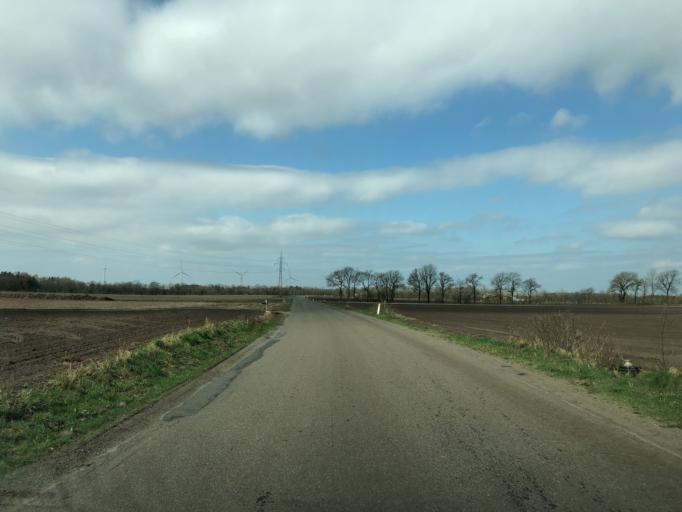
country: DK
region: South Denmark
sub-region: Vejle Kommune
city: Give
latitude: 55.9137
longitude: 9.2388
